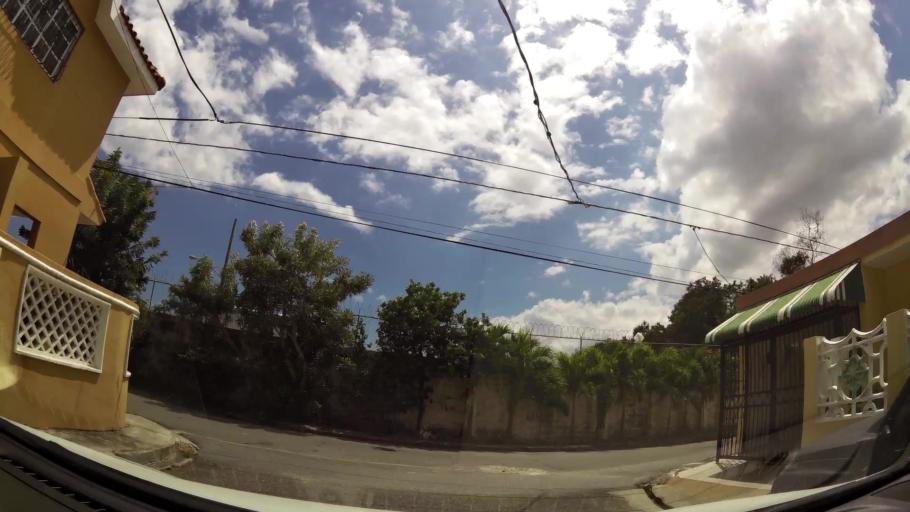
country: DO
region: San Cristobal
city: San Cristobal
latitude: 18.4128
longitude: -70.0991
